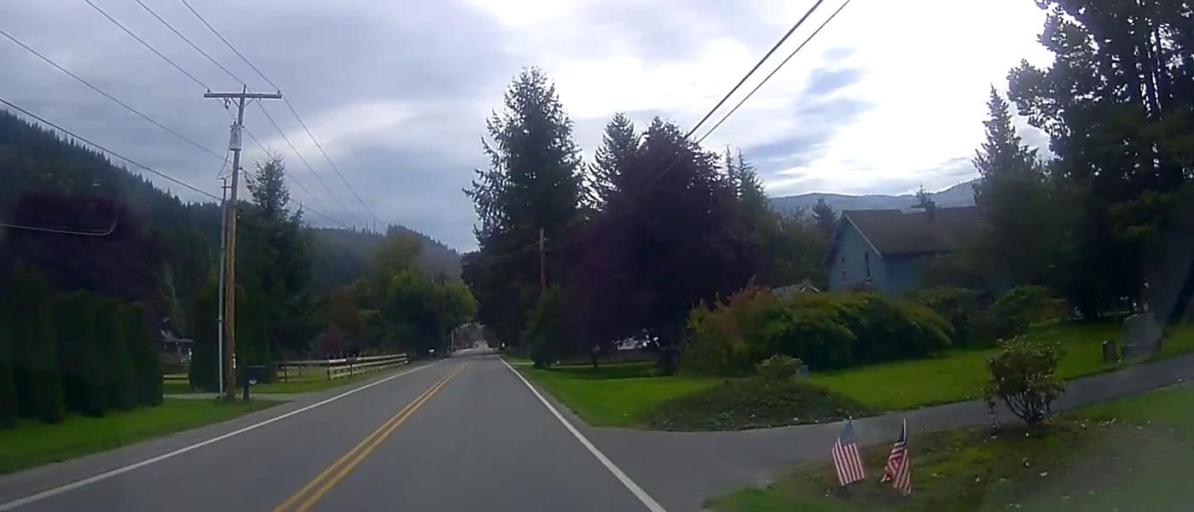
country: US
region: Washington
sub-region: Skagit County
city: Clear Lake
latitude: 48.4678
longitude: -122.2332
